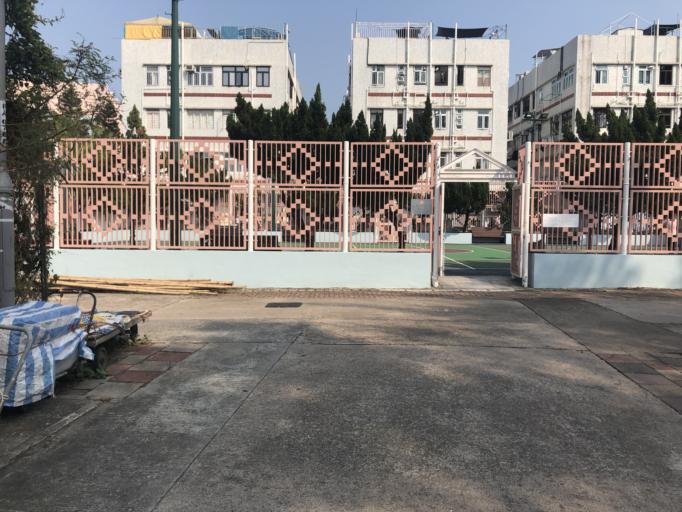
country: HK
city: Yung Shue Wan
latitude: 22.2047
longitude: 114.0256
